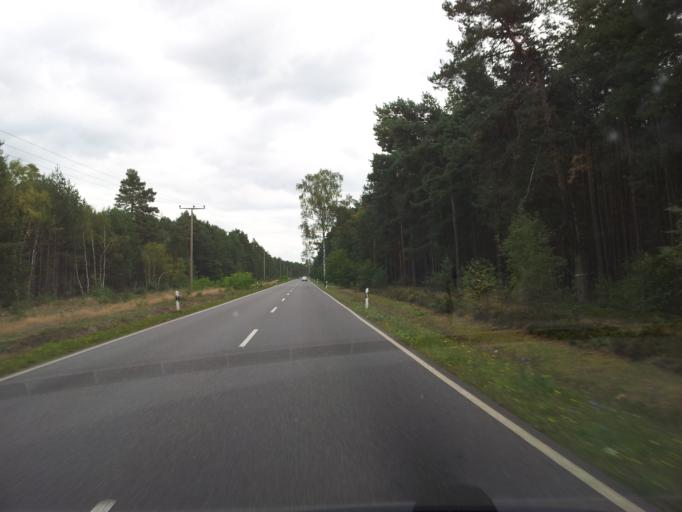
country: DE
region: Brandenburg
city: Guteborn
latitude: 51.4129
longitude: 13.9494
